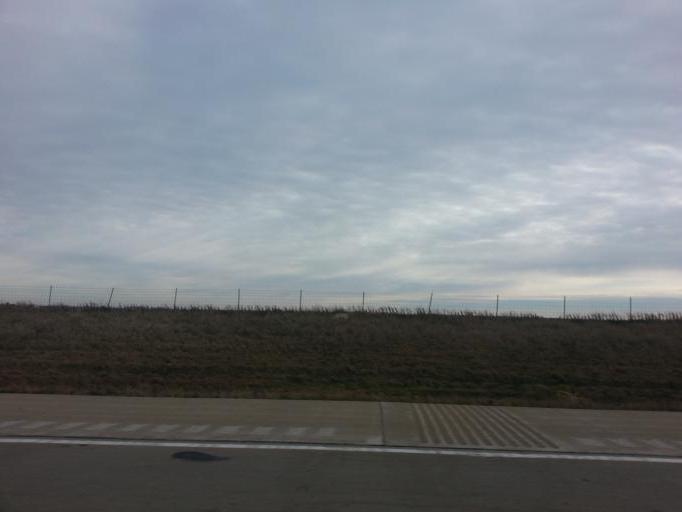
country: US
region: Illinois
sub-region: Woodford County
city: El Paso
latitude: 40.6871
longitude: -89.0288
